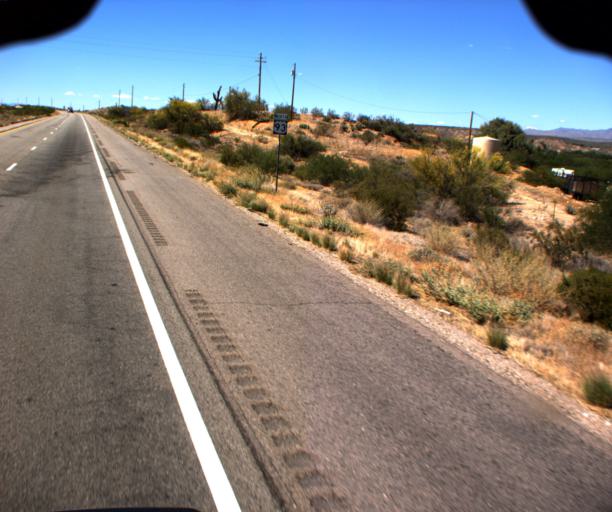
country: US
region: Arizona
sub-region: Yavapai County
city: Bagdad
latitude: 34.6707
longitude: -113.5877
